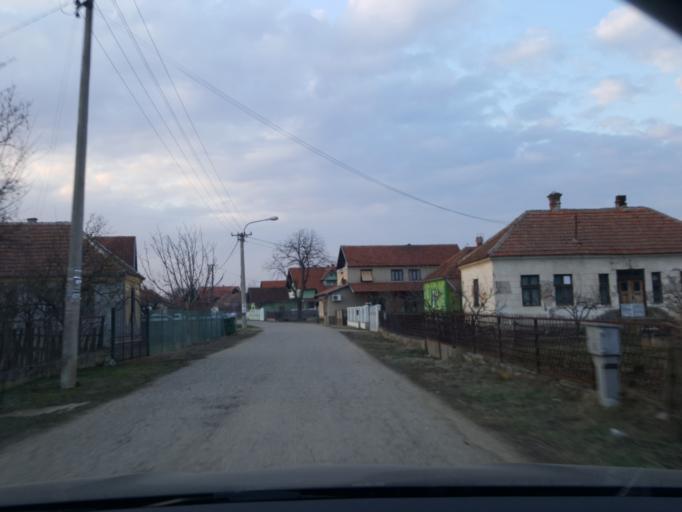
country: RS
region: Central Serbia
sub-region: Nisavski Okrug
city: Aleksinac
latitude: 43.5570
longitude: 21.6514
